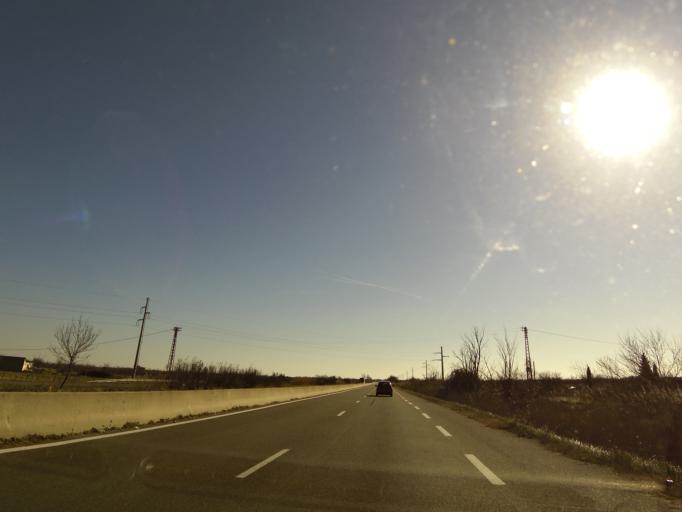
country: FR
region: Languedoc-Roussillon
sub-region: Departement du Gard
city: Aigues-Mortes
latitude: 43.6146
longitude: 4.1924
